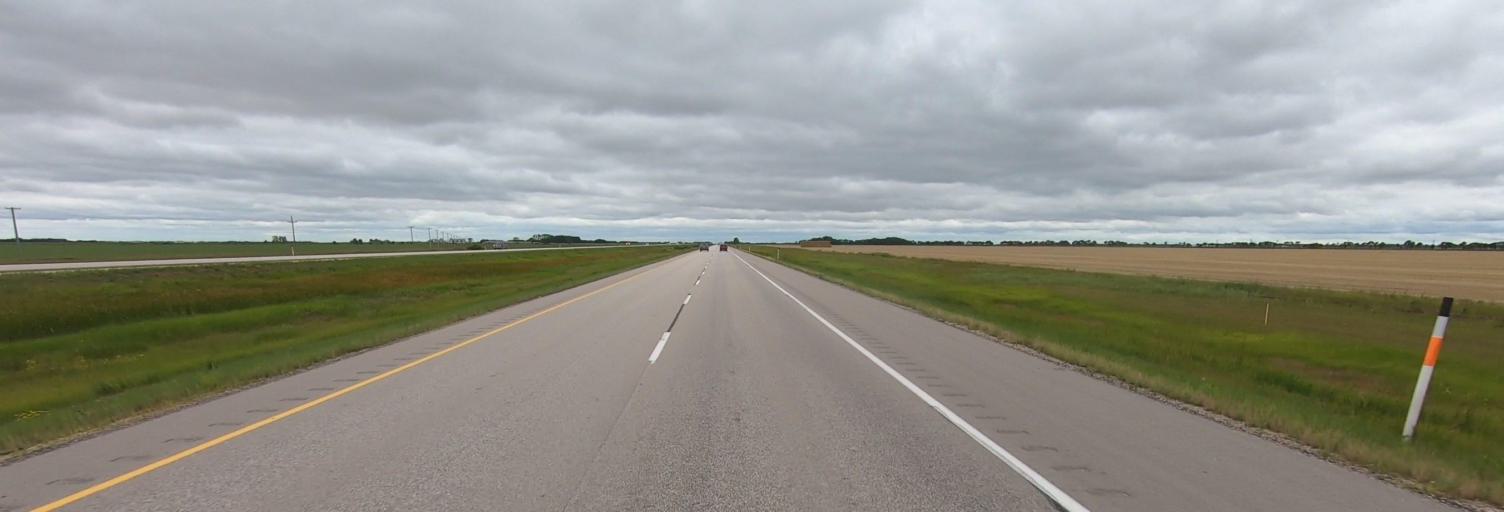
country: CA
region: Manitoba
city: Headingley
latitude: 49.9160
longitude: -97.8056
